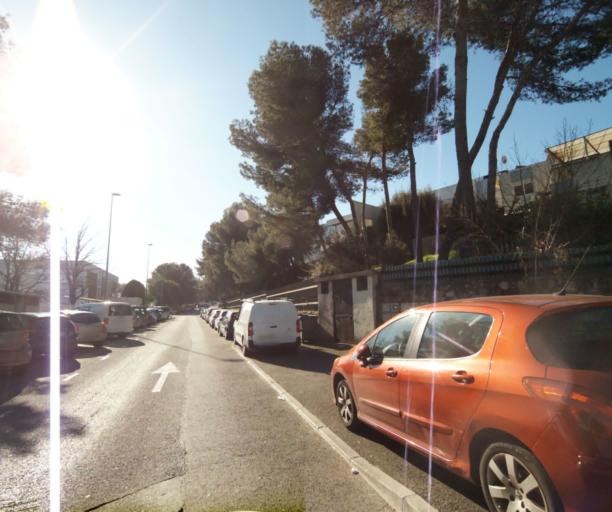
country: FR
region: Provence-Alpes-Cote d'Azur
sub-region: Departement des Alpes-Maritimes
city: Biot
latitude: 43.6058
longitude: 7.0726
